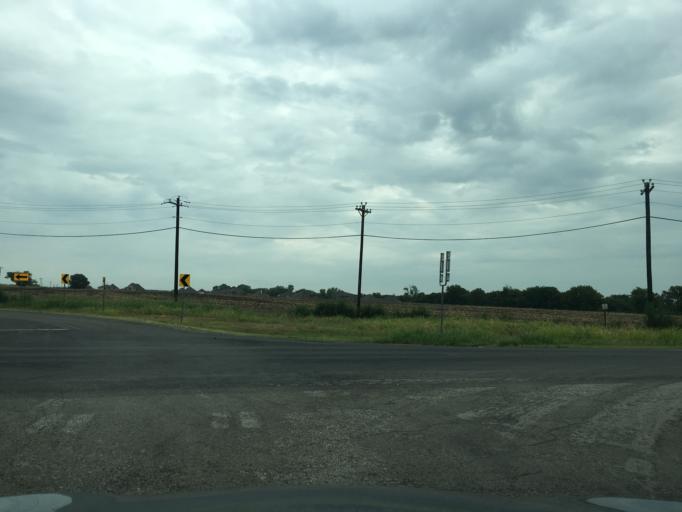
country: US
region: Texas
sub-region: Grayson County
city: Van Alstyne
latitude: 33.3999
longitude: -96.5780
